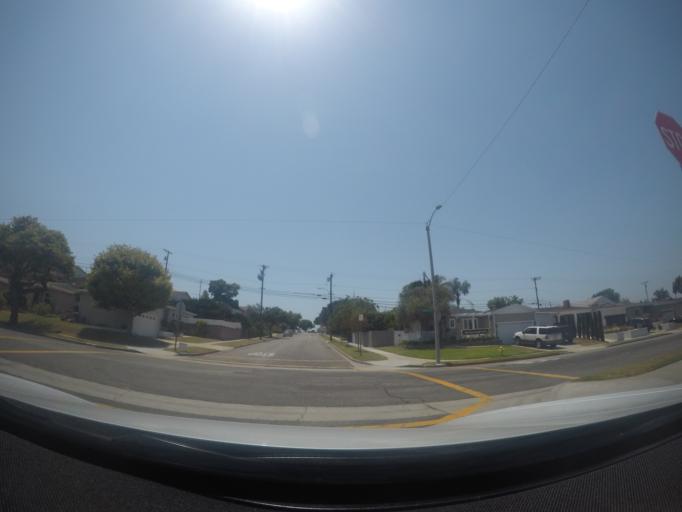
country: US
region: California
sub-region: Los Angeles County
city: Torrance
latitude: 33.8204
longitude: -118.3614
